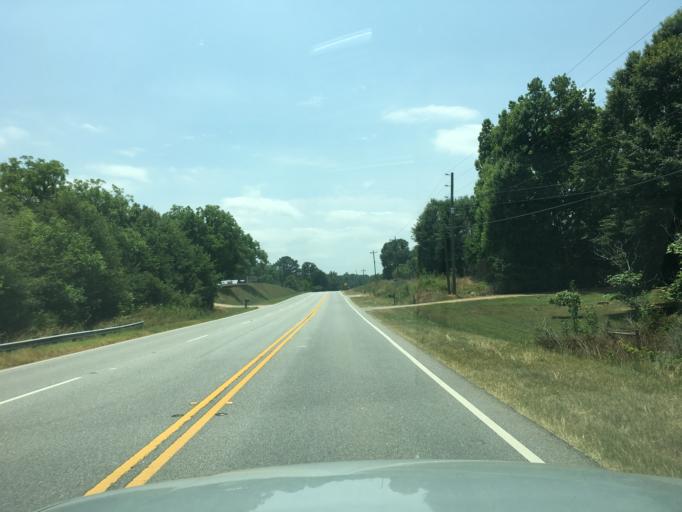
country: US
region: Georgia
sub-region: Hart County
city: Royston
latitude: 34.2713
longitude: -83.1662
